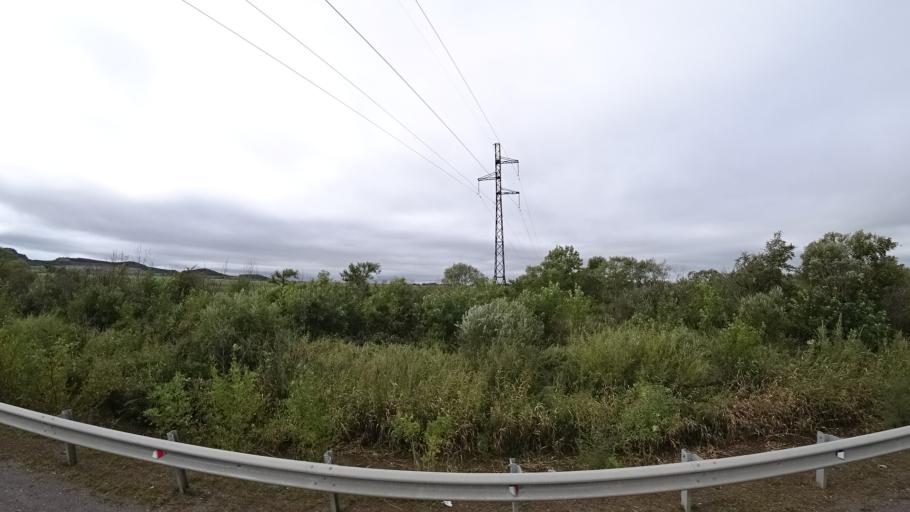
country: RU
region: Primorskiy
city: Monastyrishche
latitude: 44.1811
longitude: 132.4415
